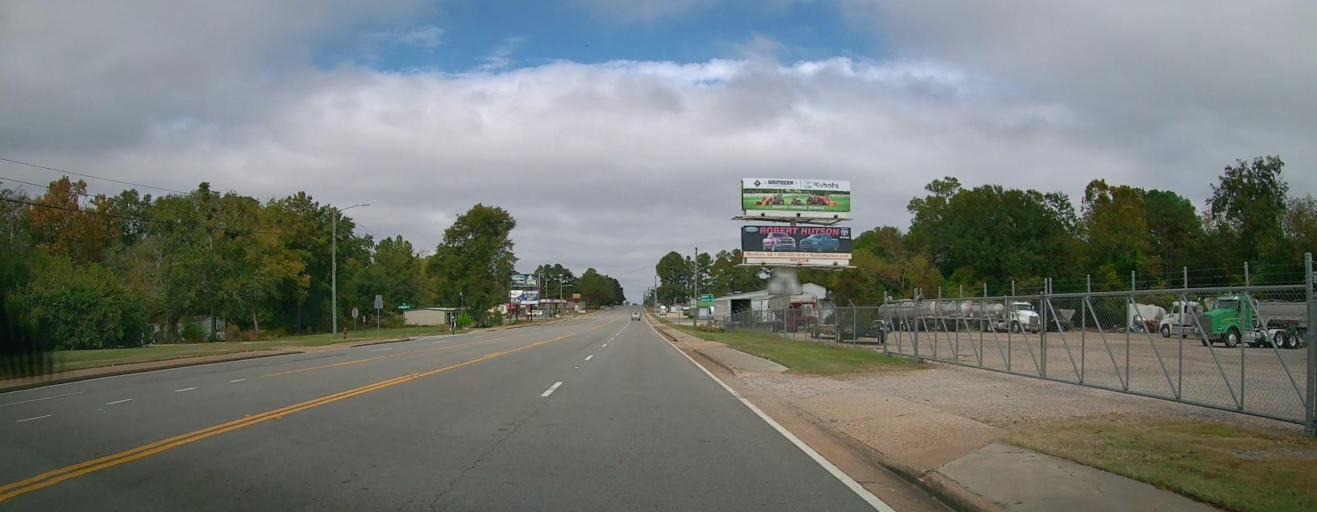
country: US
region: Georgia
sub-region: Colquitt County
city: Moultrie
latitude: 31.0118
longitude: -83.8664
